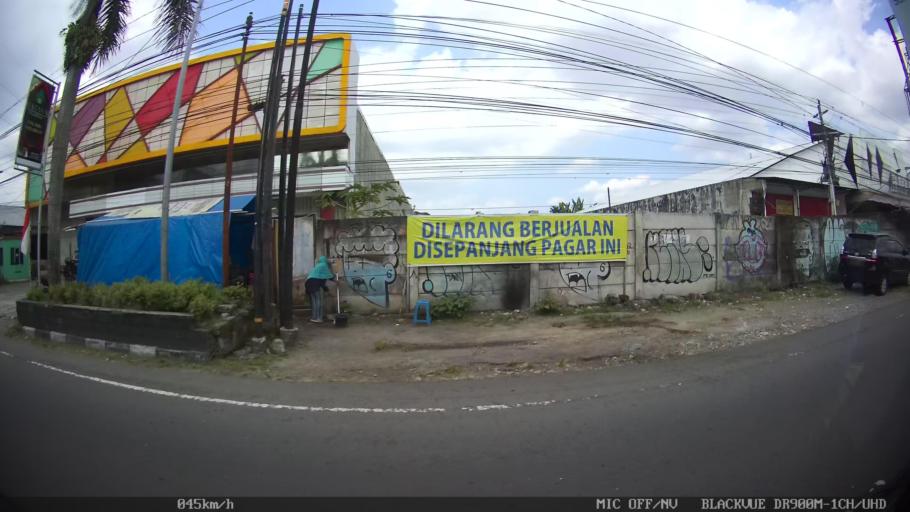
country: ID
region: Daerah Istimewa Yogyakarta
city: Melati
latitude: -7.7557
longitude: 110.3621
